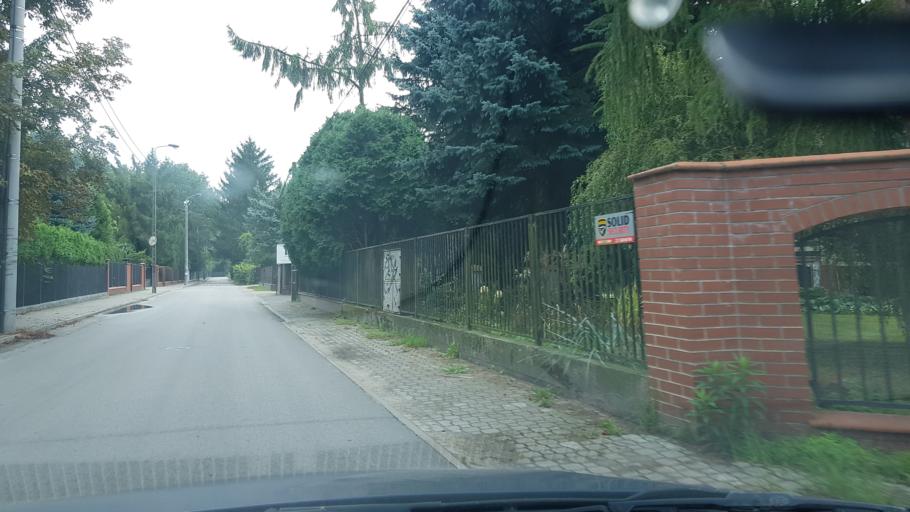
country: PL
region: Masovian Voivodeship
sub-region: Powiat piaseczynski
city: Konstancin-Jeziorna
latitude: 52.1030
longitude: 21.1054
